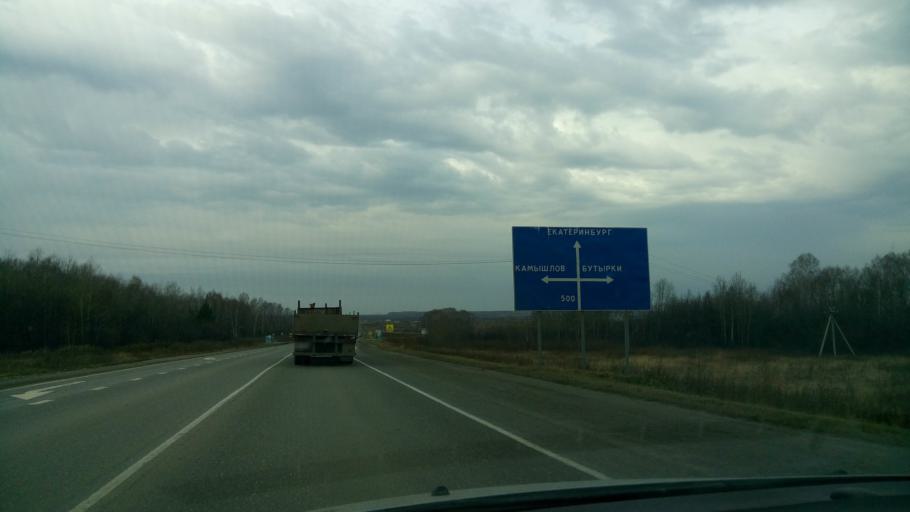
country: RU
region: Sverdlovsk
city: Kamyshlov
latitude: 56.8684
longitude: 62.7501
